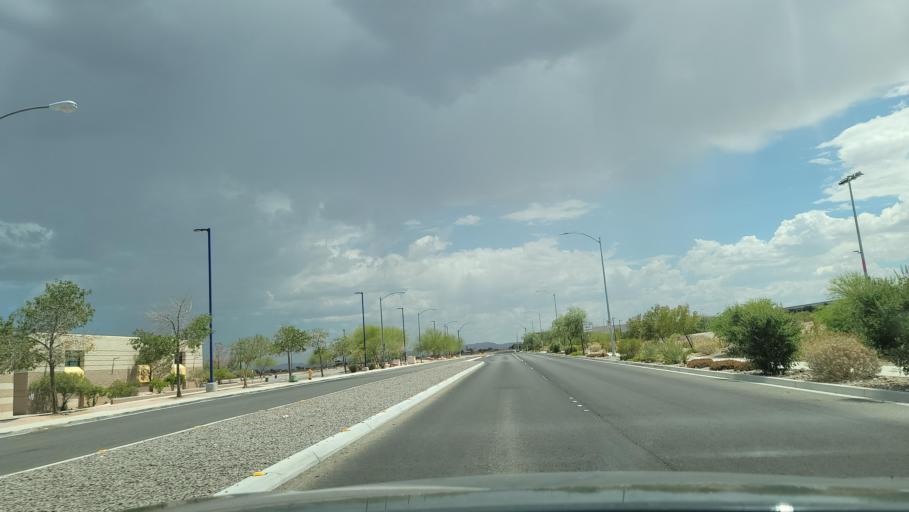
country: US
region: Nevada
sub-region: Clark County
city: Enterprise
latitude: 36.0506
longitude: -115.2702
